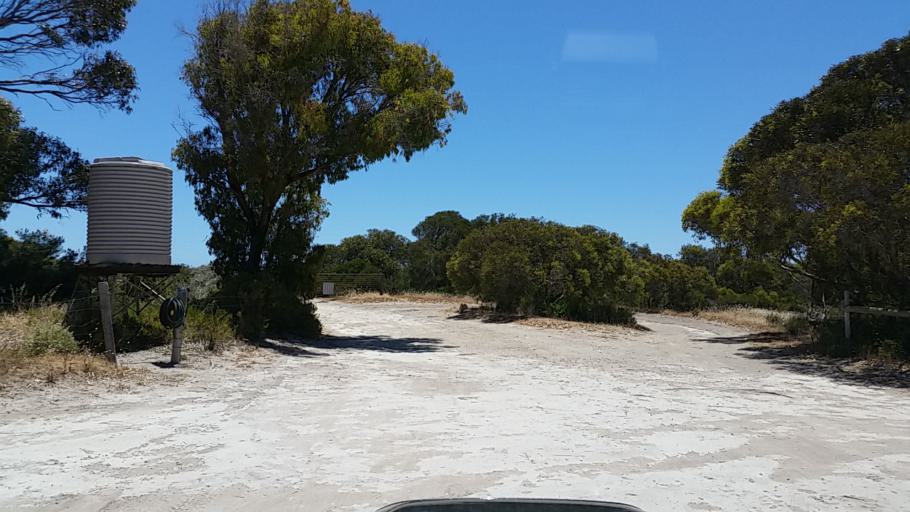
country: AU
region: South Australia
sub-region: Yorke Peninsula
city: Honiton
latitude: -35.2314
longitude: 137.1254
